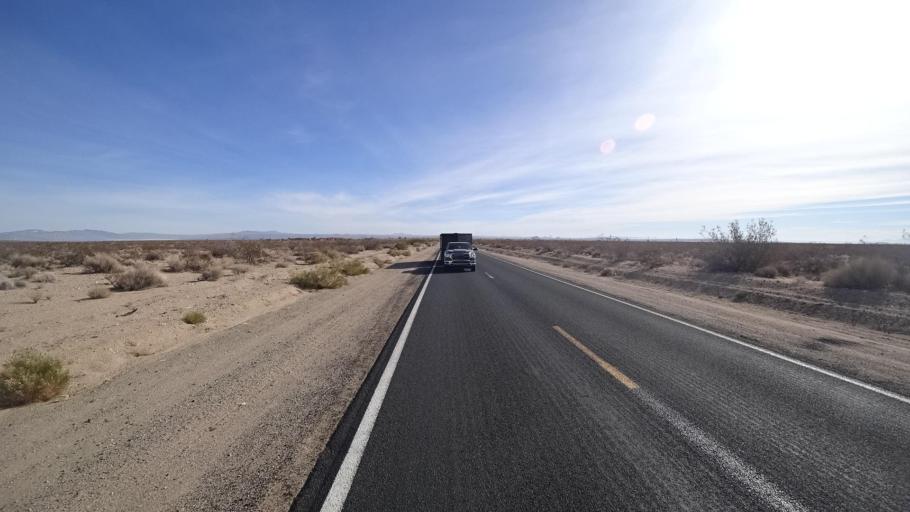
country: US
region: California
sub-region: Kern County
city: Mojave
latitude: 35.1254
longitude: -118.1339
